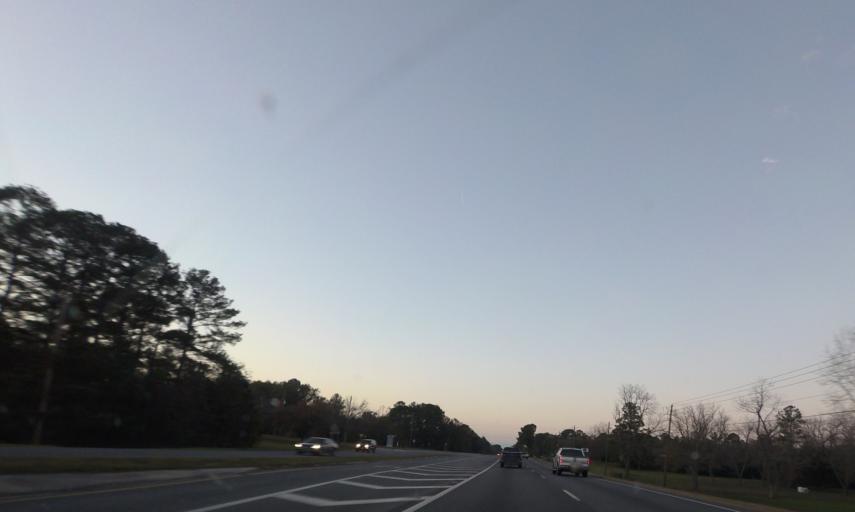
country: US
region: Georgia
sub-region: Houston County
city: Centerville
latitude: 32.7051
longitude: -83.6420
